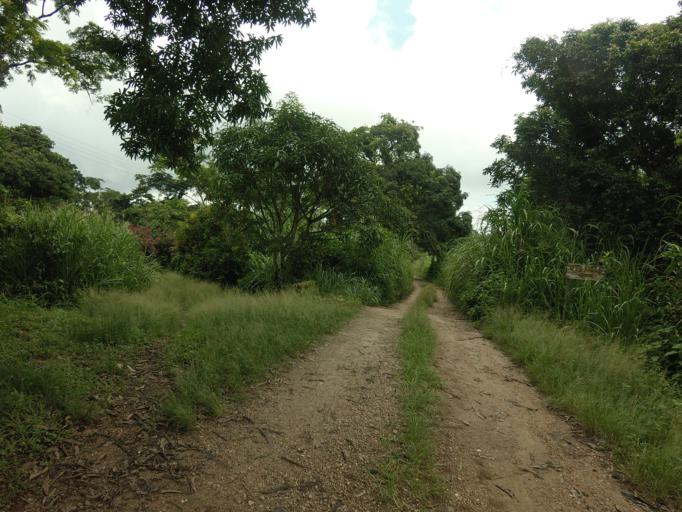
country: TG
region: Plateaux
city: Kpalime
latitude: 6.8432
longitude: 0.4451
